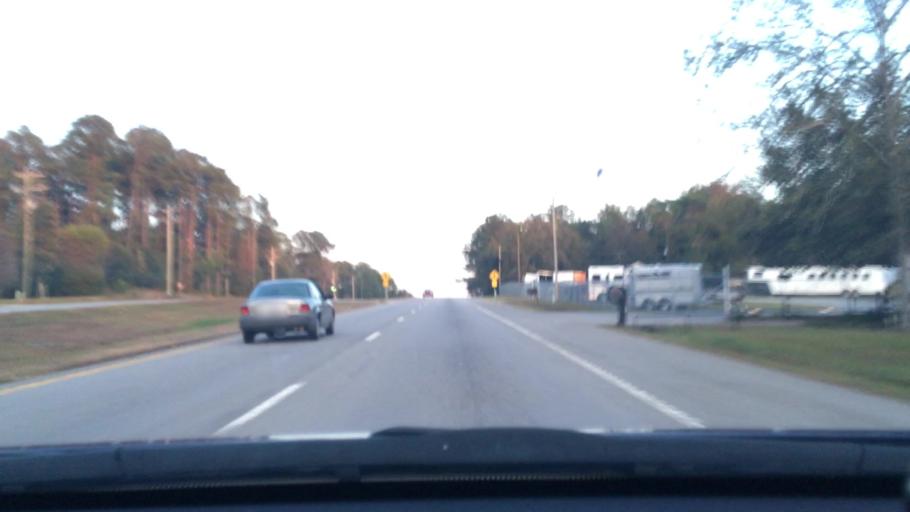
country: US
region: South Carolina
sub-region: Richland County
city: Gadsden
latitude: 33.9437
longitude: -80.7430
